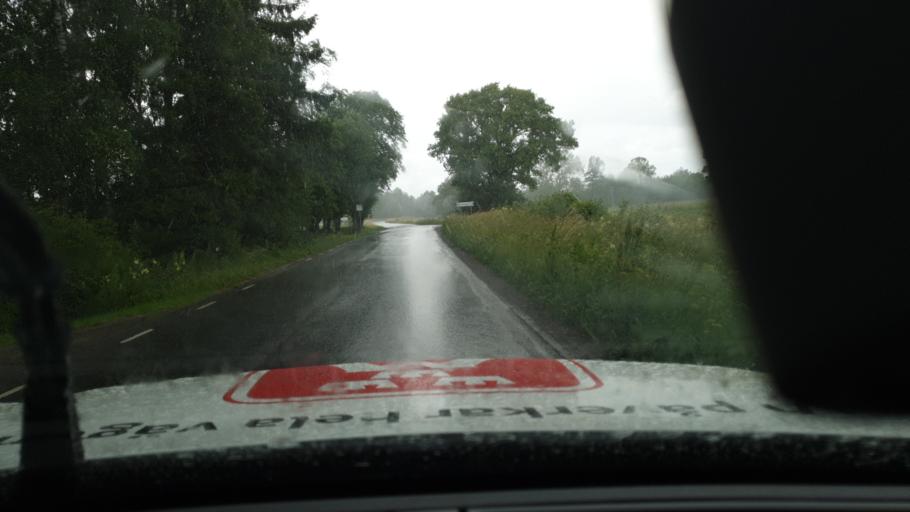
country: SE
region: Vaestra Goetaland
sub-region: Falkopings Kommun
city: Akarp
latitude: 58.2284
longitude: 13.6057
